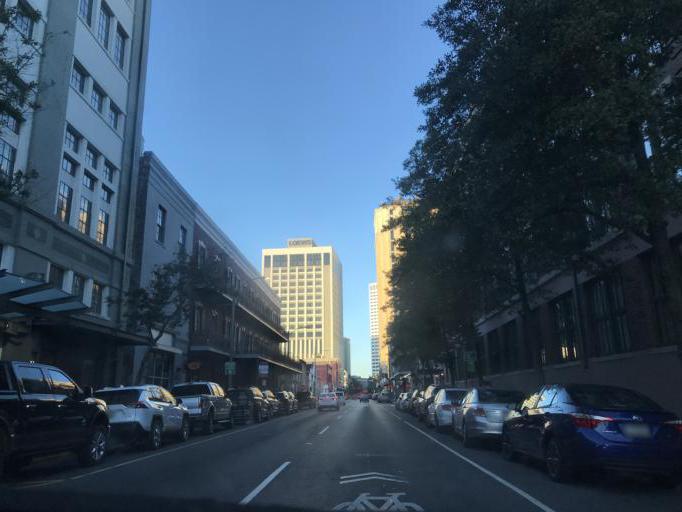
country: US
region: Louisiana
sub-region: Orleans Parish
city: New Orleans
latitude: 29.9454
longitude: -90.0658
